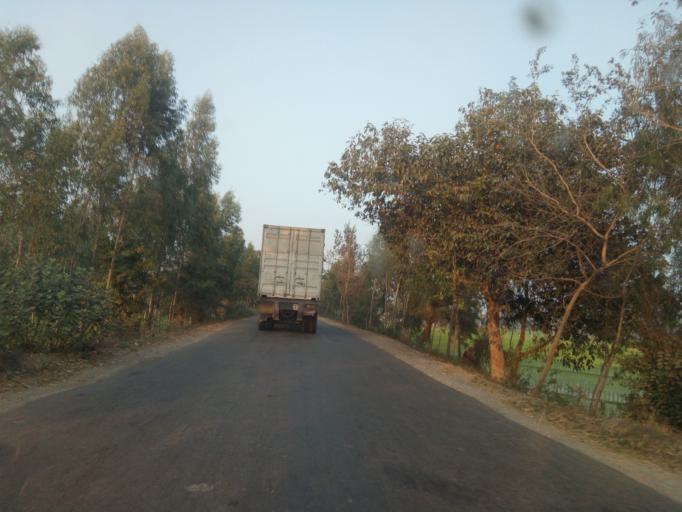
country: BD
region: Rajshahi
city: Bogra
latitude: 24.5504
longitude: 89.1915
